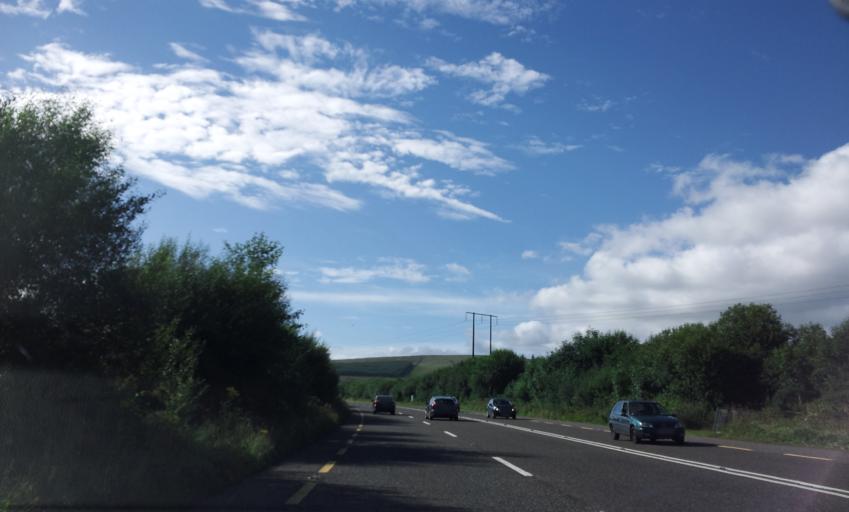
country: IE
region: Munster
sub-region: County Cork
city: Millstreet
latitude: 51.9575
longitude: -9.1919
